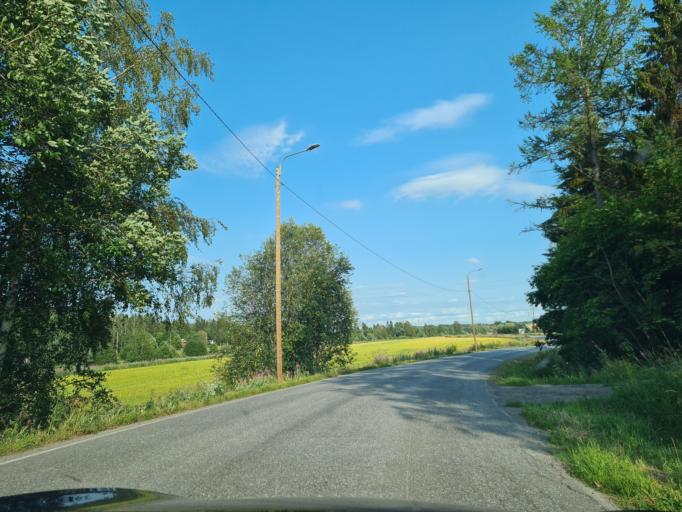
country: FI
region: Ostrobothnia
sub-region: Vaasa
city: Ristinummi
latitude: 63.0307
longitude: 21.8208
